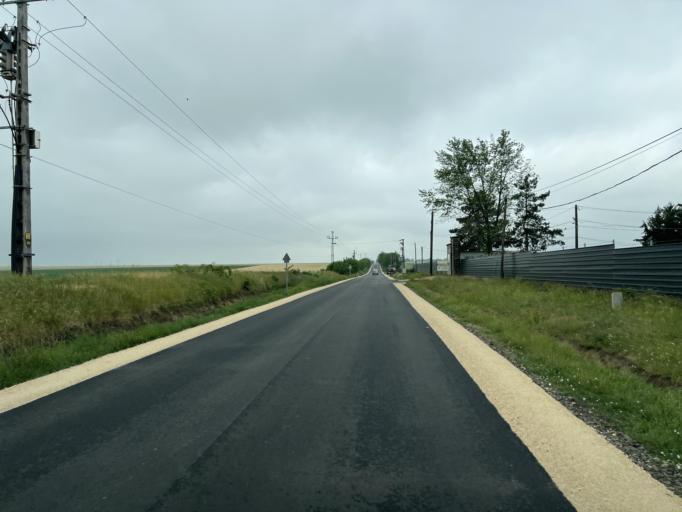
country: HU
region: Pest
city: Galgaheviz
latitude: 47.5940
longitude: 19.5772
